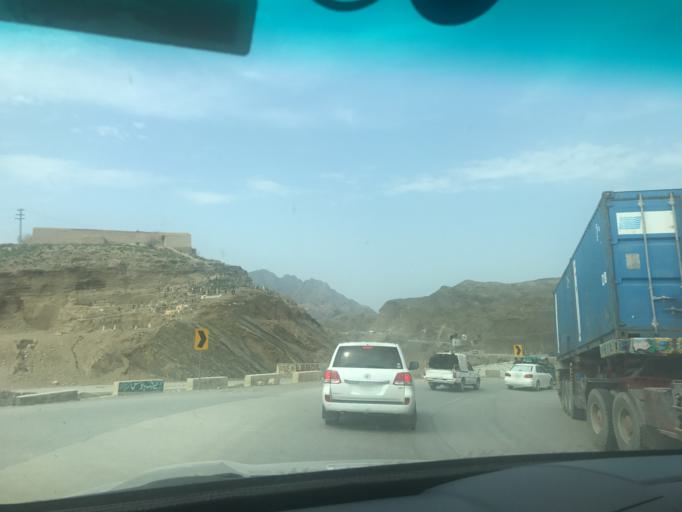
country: PK
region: Federally Administered Tribal Areas
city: Landi Kotal
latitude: 34.1008
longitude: 71.1373
